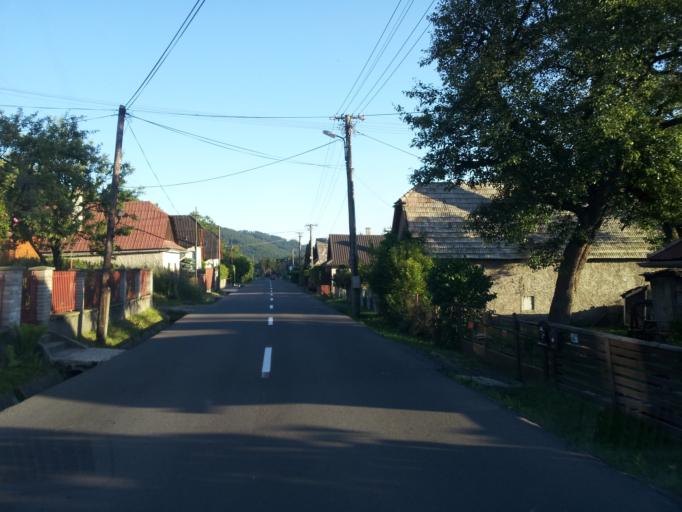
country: SK
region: Banskobystricky
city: Svaety Anton
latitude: 48.4167
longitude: 18.9395
